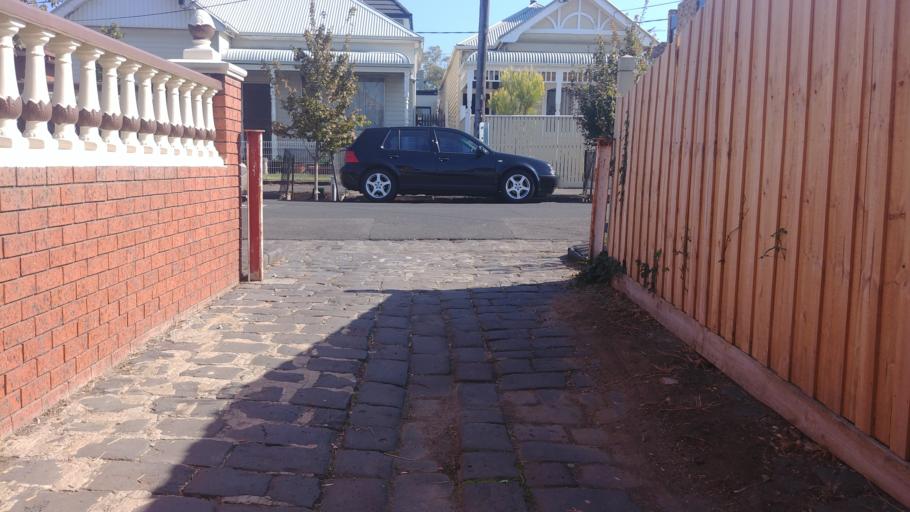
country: AU
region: Victoria
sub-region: Moreland
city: Brunswick
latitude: -37.7625
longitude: 144.9695
